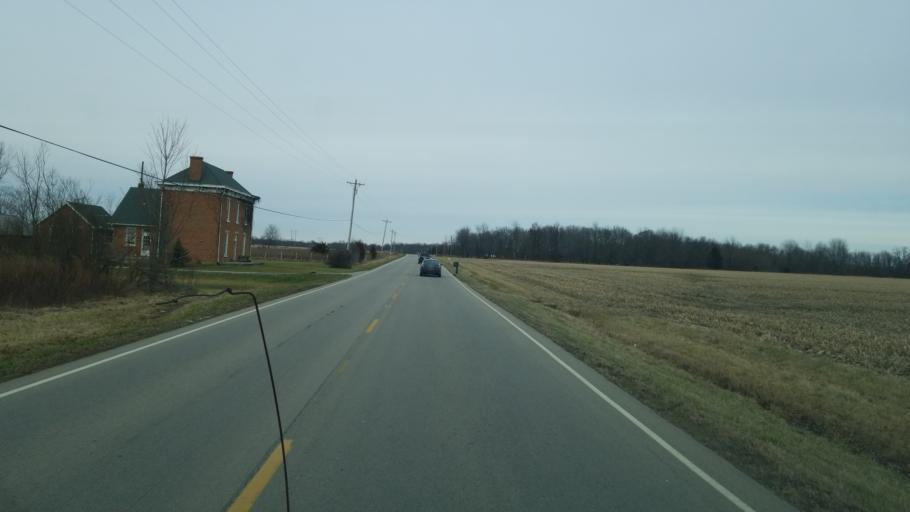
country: US
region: Ohio
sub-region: Highland County
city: Hillsboro
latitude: 39.0956
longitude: -83.6797
